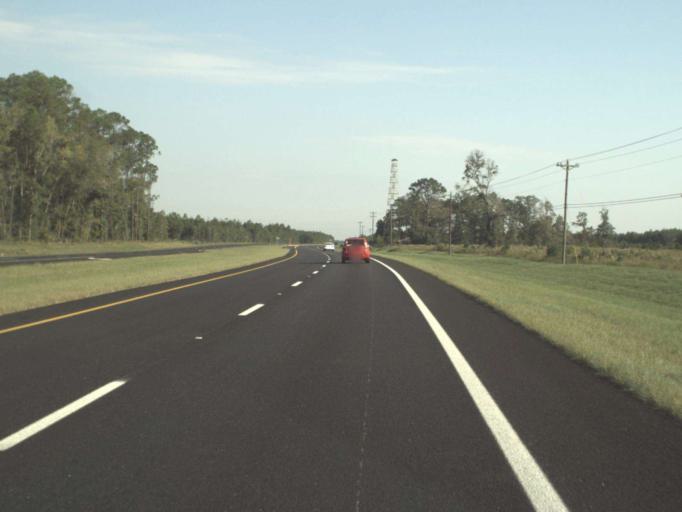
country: US
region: Florida
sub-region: Bay County
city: Laguna Beach
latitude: 30.4875
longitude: -85.8422
